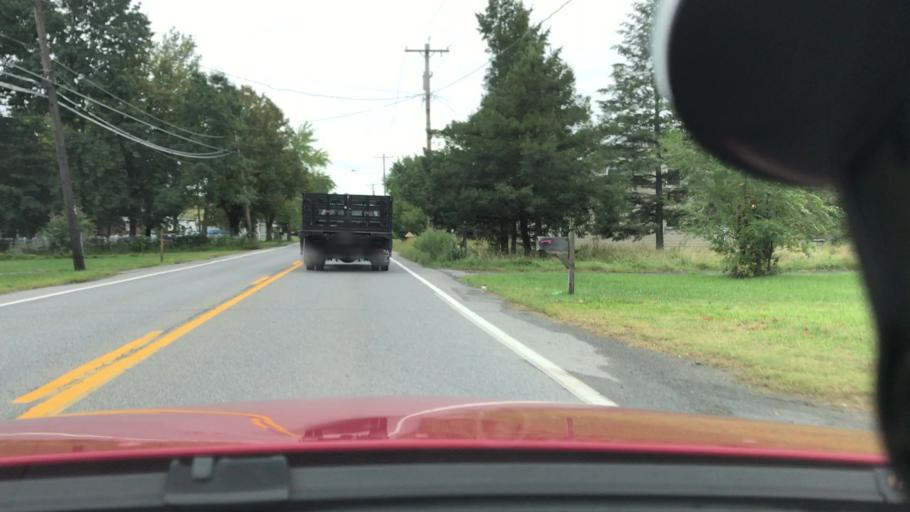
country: US
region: New York
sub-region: Saratoga County
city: Waterford
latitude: 42.8076
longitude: -73.6671
